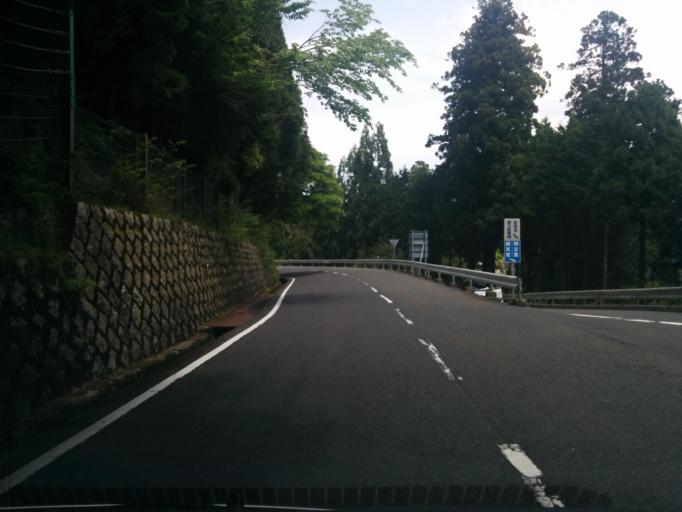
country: JP
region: Shiga Prefecture
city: Otsu-shi
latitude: 35.0667
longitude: 135.8422
